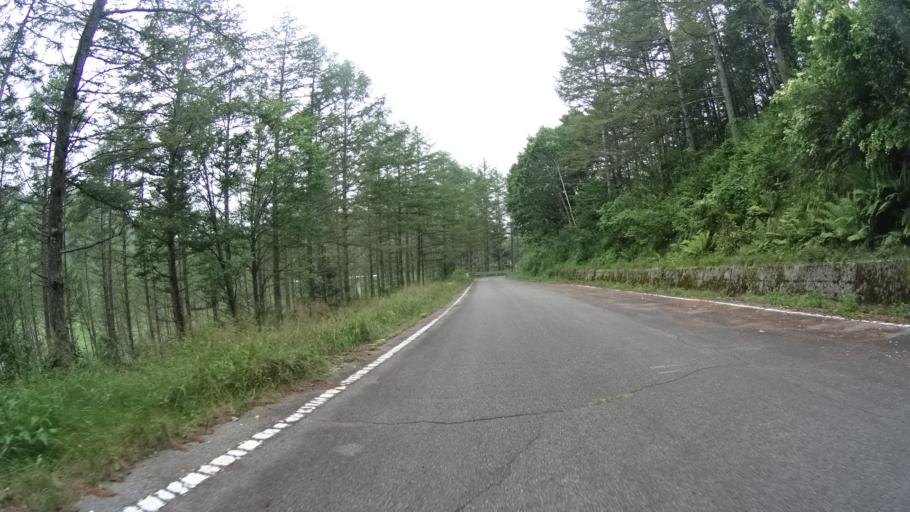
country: JP
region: Yamanashi
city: Kofu-shi
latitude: 35.8292
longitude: 138.5780
